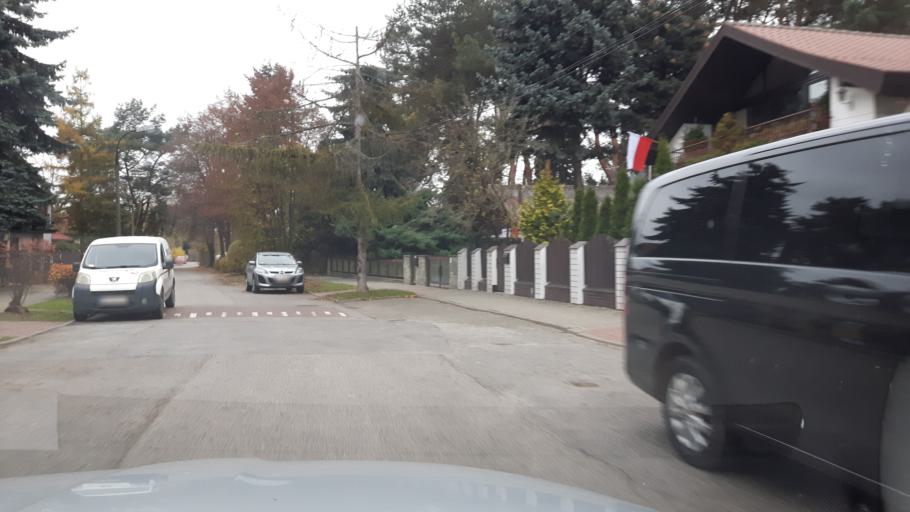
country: PL
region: Masovian Voivodeship
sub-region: Warszawa
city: Targowek
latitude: 52.2914
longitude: 21.0638
